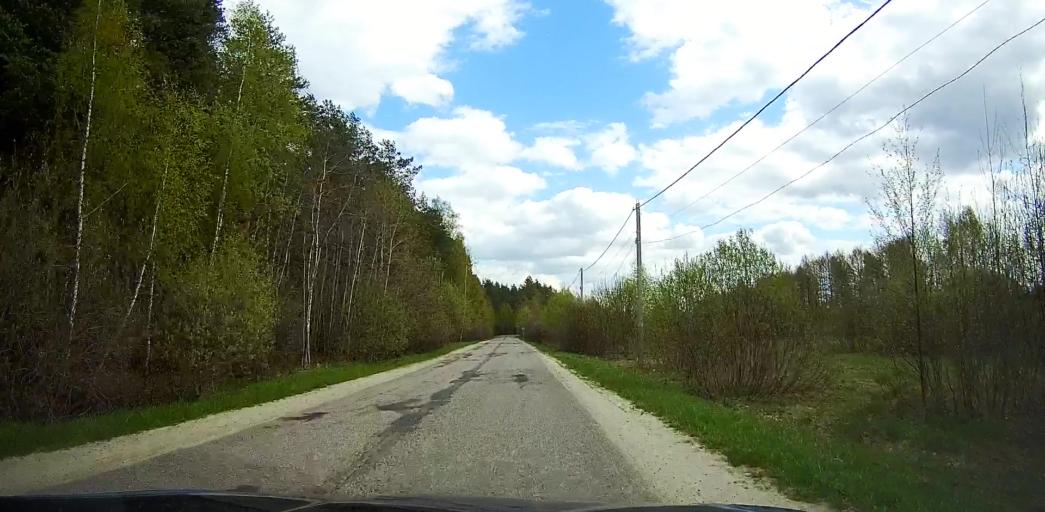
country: RU
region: Moskovskaya
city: Davydovo
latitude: 55.6454
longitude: 38.7703
